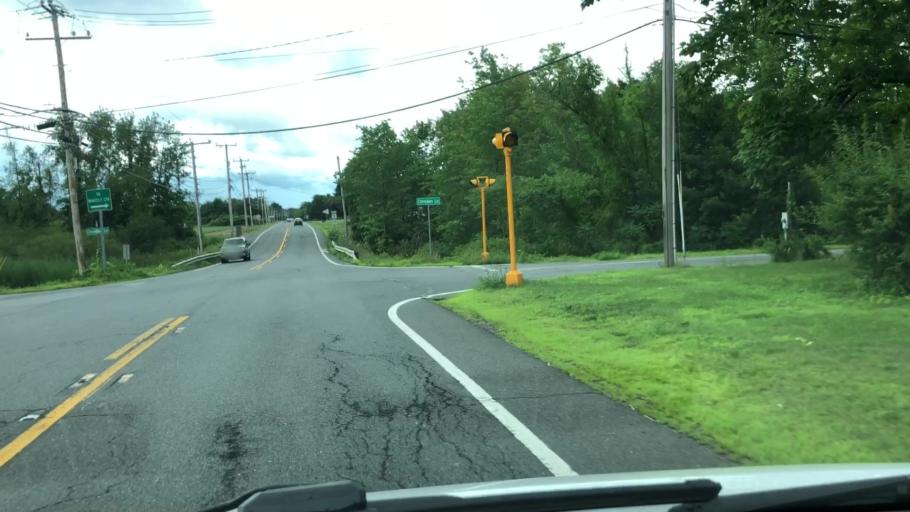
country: US
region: Massachusetts
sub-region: Franklin County
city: Whately
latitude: 42.4449
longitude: -72.6258
